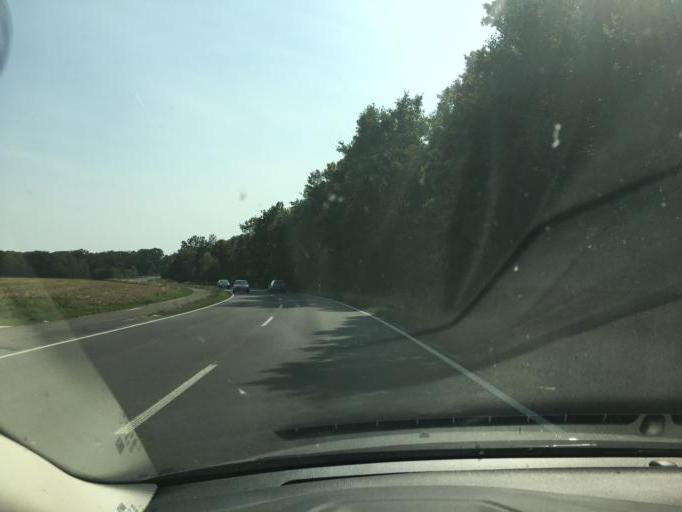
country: DE
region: Saxony-Anhalt
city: Plotzky
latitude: 52.0471
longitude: 11.7997
